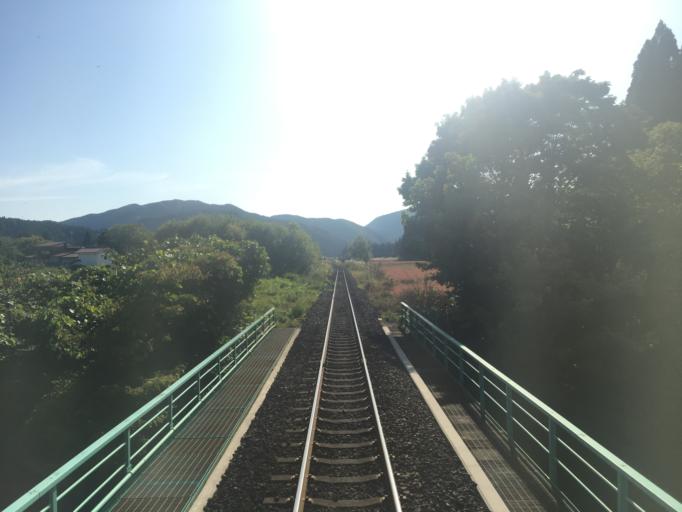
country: JP
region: Akita
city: Kakunodatemachi
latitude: 39.7462
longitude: 140.5928
